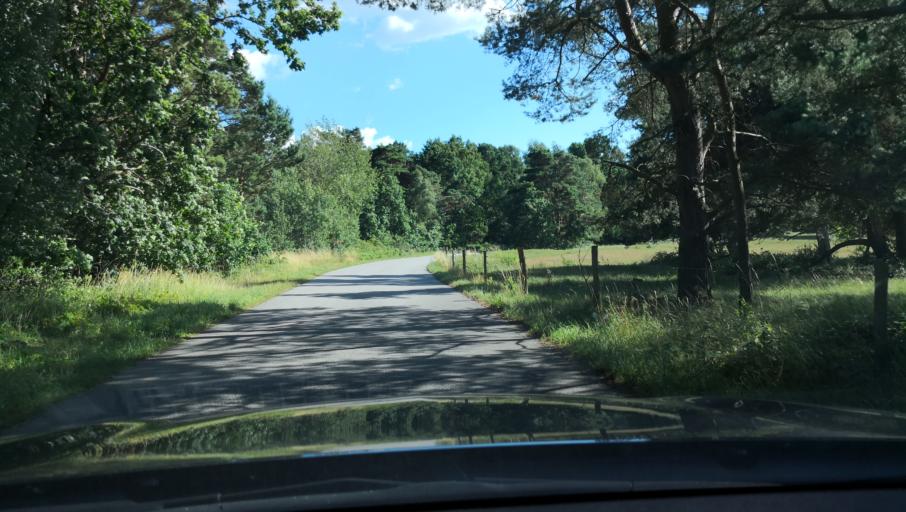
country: SE
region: Skane
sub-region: Simrishamns Kommun
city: Kivik
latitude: 55.7865
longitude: 14.1960
